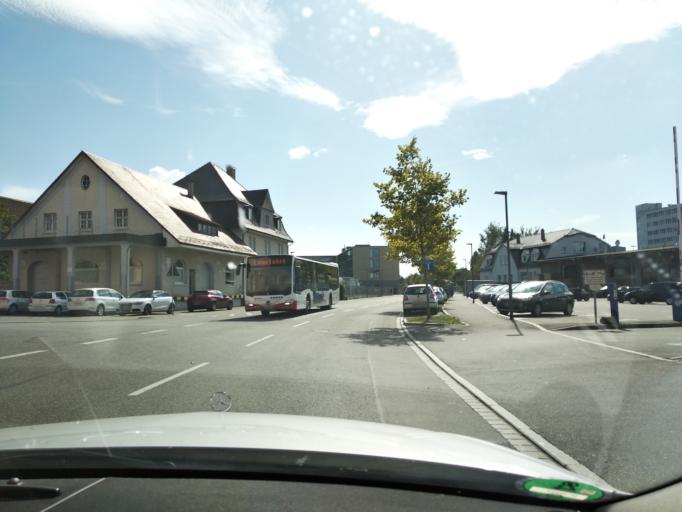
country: DE
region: Baden-Wuerttemberg
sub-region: Tuebingen Region
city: Ravensburg
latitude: 47.7871
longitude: 9.6089
